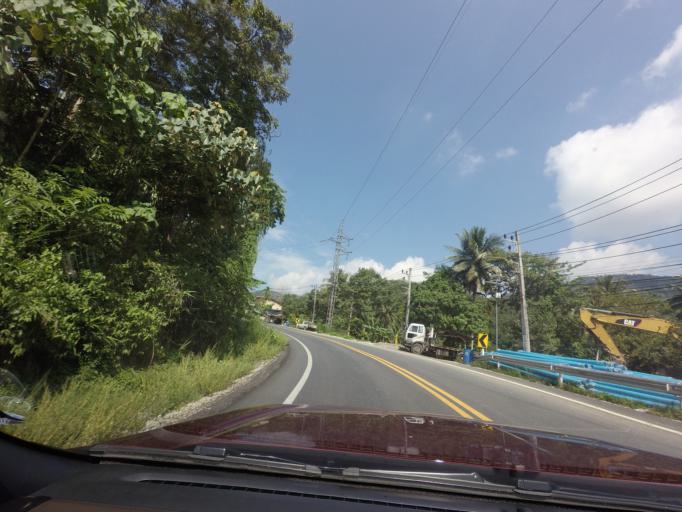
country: TH
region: Yala
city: Betong
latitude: 5.9105
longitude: 101.1527
